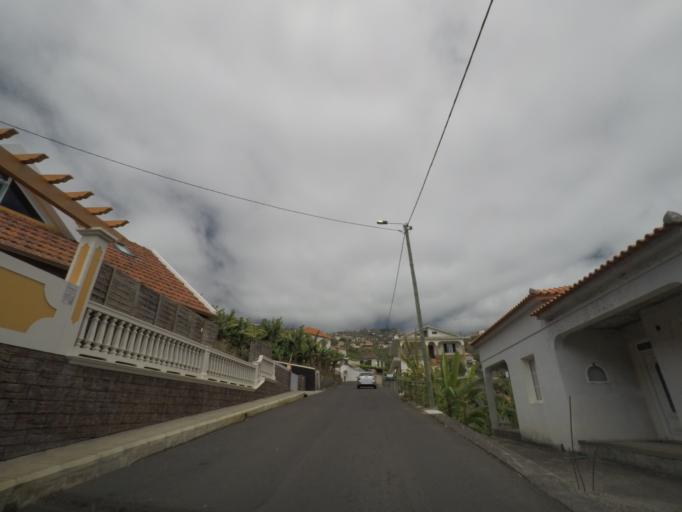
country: PT
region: Madeira
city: Ponta do Sol
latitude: 32.6857
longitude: -17.1041
